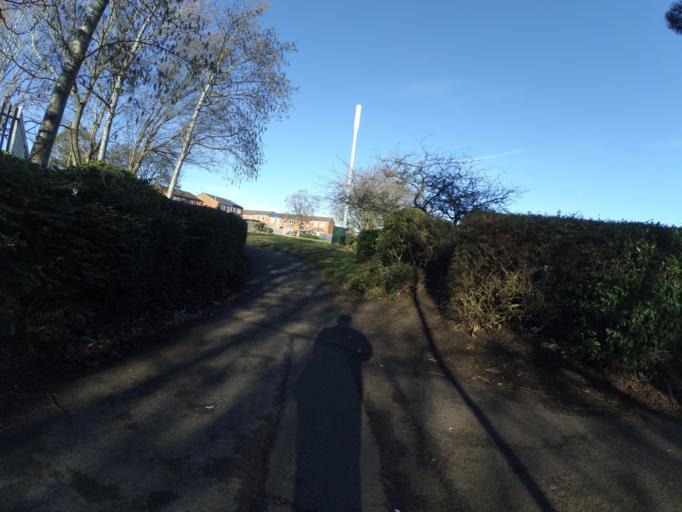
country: GB
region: England
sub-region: Warwickshire
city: Rugby
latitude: 52.3912
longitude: -1.2435
